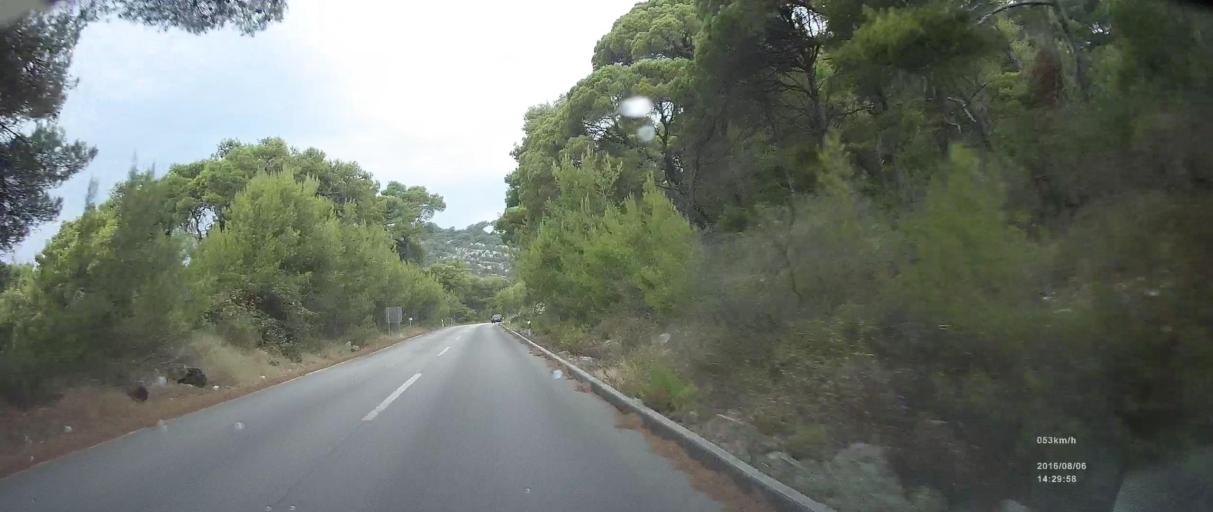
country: HR
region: Dubrovacko-Neretvanska
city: Ston
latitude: 42.7077
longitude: 17.7309
